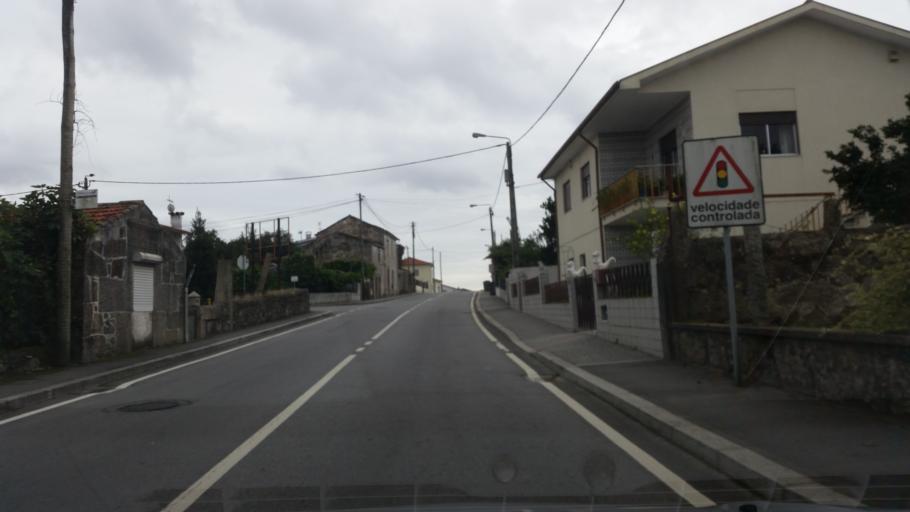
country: PT
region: Porto
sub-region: Valongo
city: Alfena
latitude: 41.2427
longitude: -8.5396
